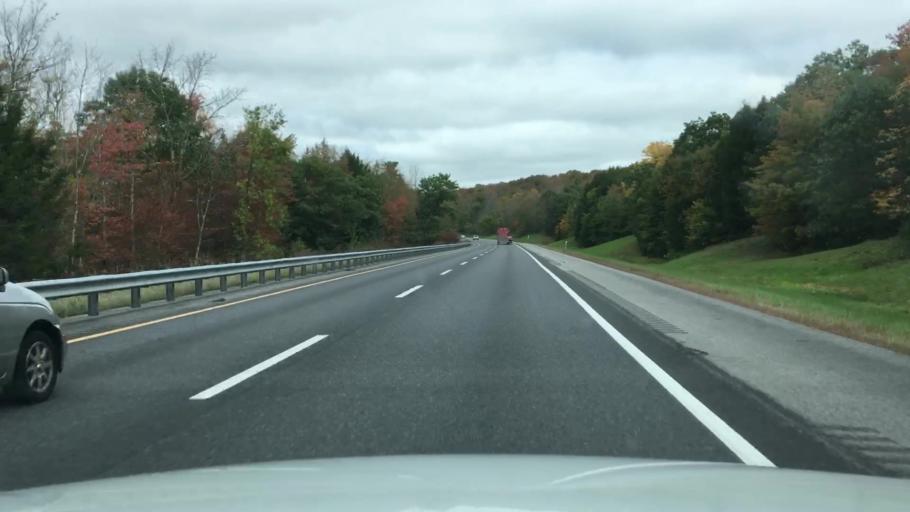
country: US
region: Maine
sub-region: Sagadahoc County
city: Richmond
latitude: 44.0631
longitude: -69.8819
